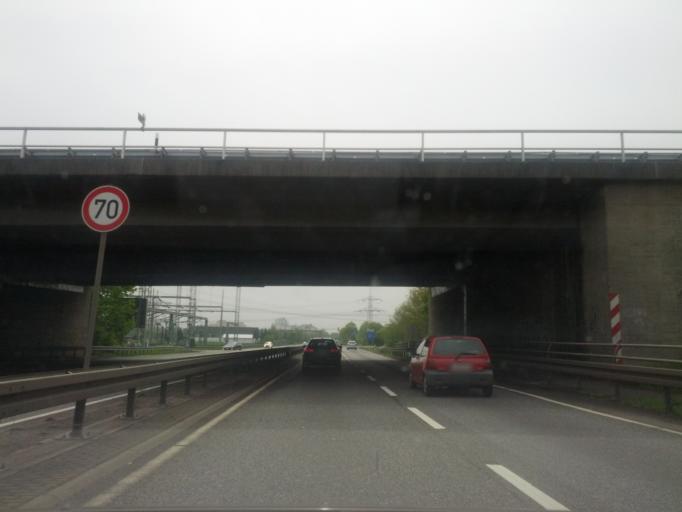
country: DE
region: Hesse
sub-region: Regierungsbezirk Giessen
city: Giessen
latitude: 50.6071
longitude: 8.6526
